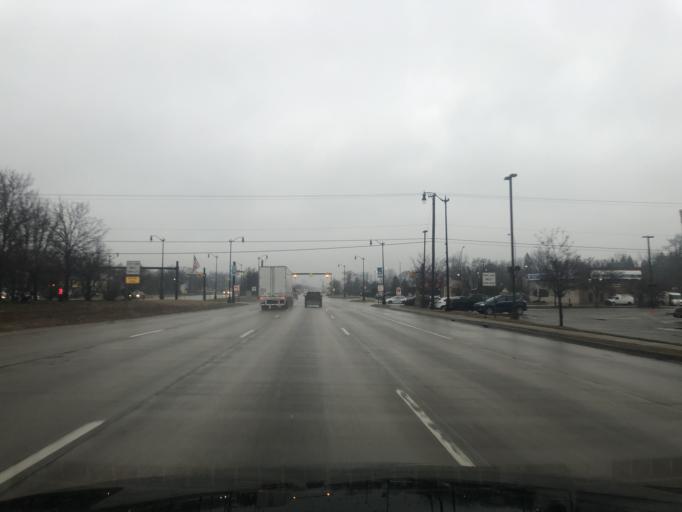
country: US
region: Michigan
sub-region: Wayne County
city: Taylor
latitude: 42.1965
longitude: -83.2676
